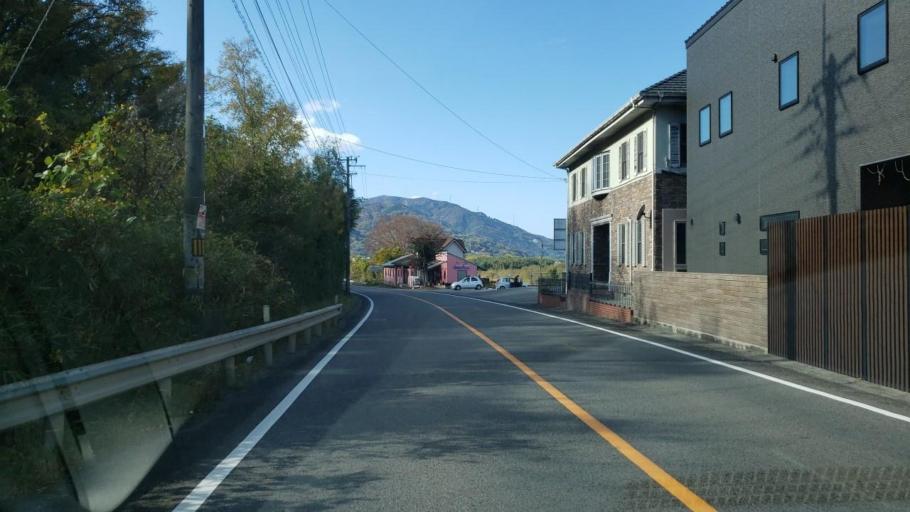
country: JP
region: Tokushima
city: Wakimachi
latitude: 34.0635
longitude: 134.1915
